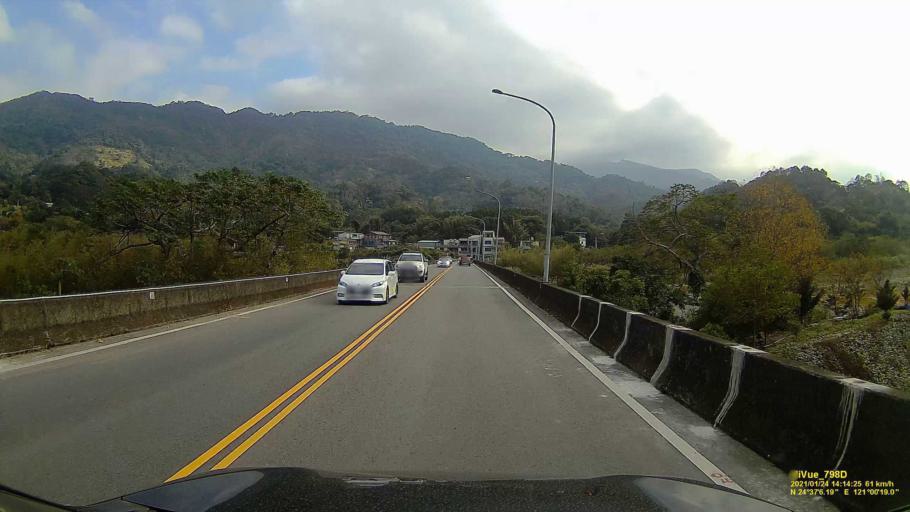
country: TW
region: Taiwan
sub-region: Hsinchu
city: Hsinchu
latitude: 24.6182
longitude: 121.0054
